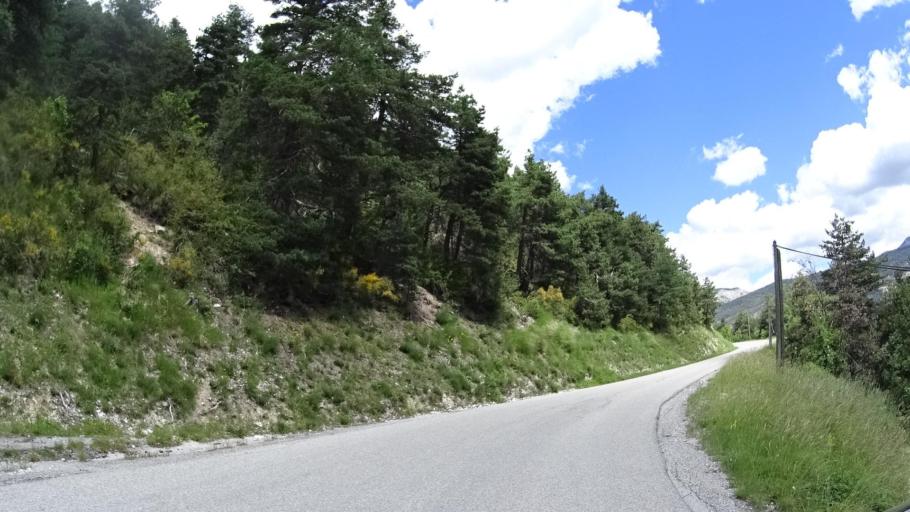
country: FR
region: Provence-Alpes-Cote d'Azur
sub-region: Departement des Alpes-de-Haute-Provence
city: Annot
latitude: 44.0180
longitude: 6.6224
